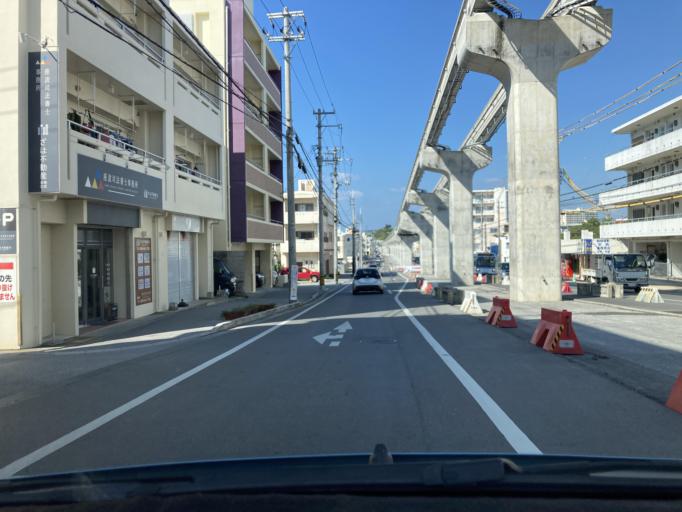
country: JP
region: Okinawa
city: Ginowan
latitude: 26.2286
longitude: 127.7291
